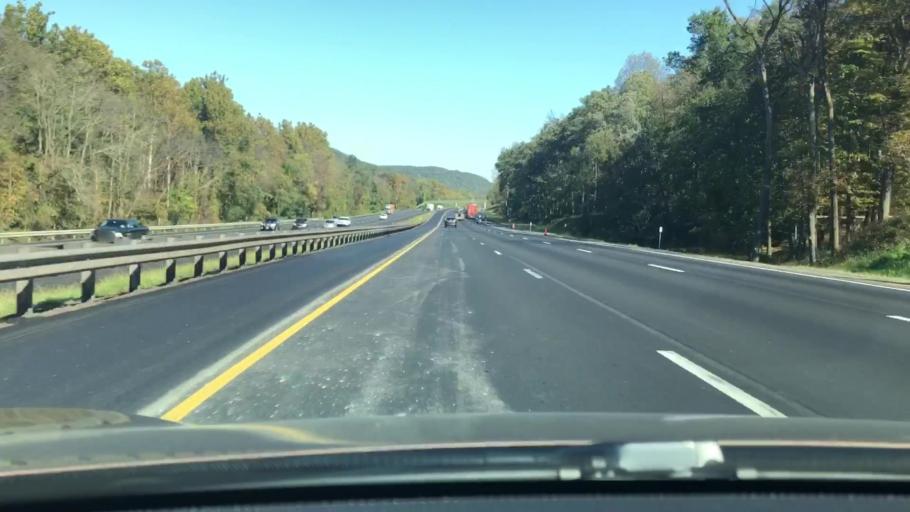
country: US
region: New York
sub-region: Orange County
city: Harriman
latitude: 41.2389
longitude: -74.1723
